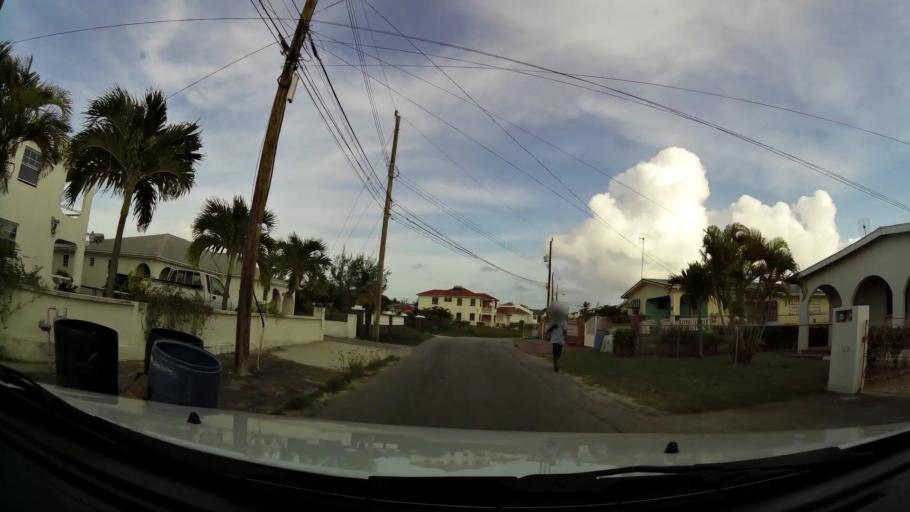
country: BB
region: Christ Church
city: Oistins
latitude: 13.0702
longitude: -59.5375
